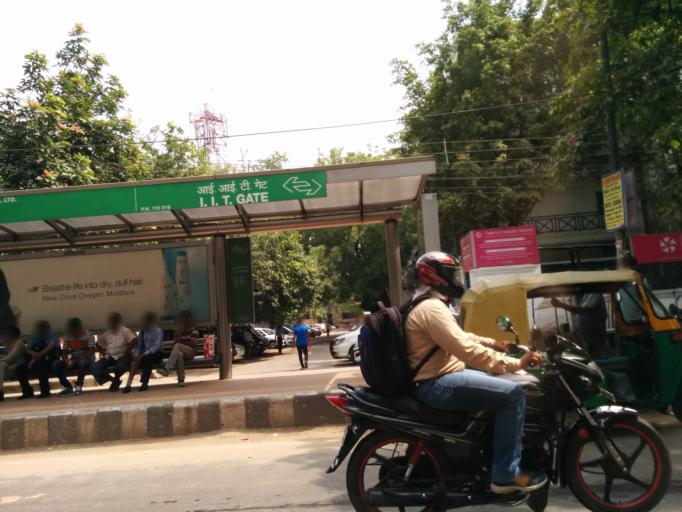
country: IN
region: NCT
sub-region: New Delhi
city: New Delhi
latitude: 28.5459
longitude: 77.1970
